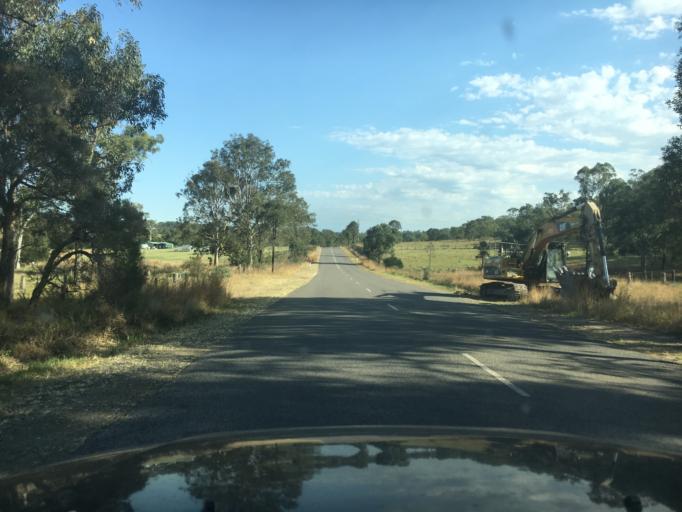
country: AU
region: New South Wales
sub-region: Cessnock
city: Branxton
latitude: -32.5879
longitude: 151.3302
